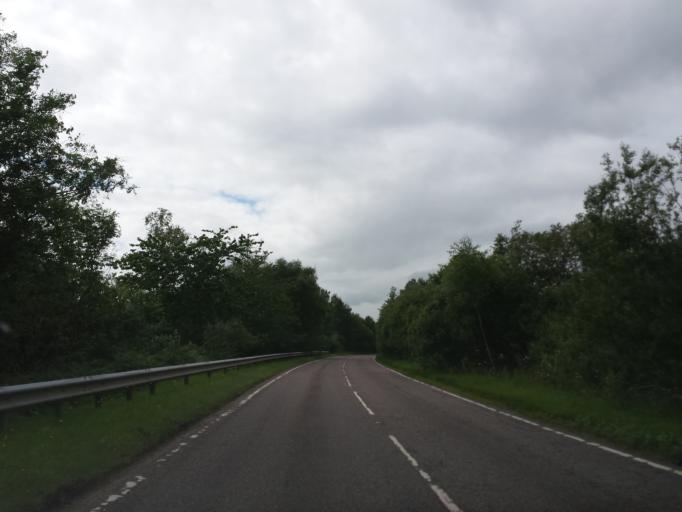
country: GB
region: Scotland
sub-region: Highland
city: Fort William
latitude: 56.8543
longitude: -5.2603
